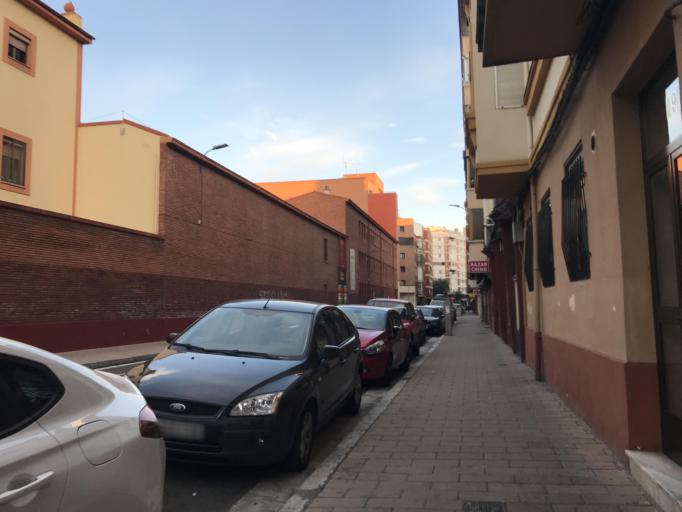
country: ES
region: Castille and Leon
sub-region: Provincia de Valladolid
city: Valladolid
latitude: 41.6525
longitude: -4.7140
